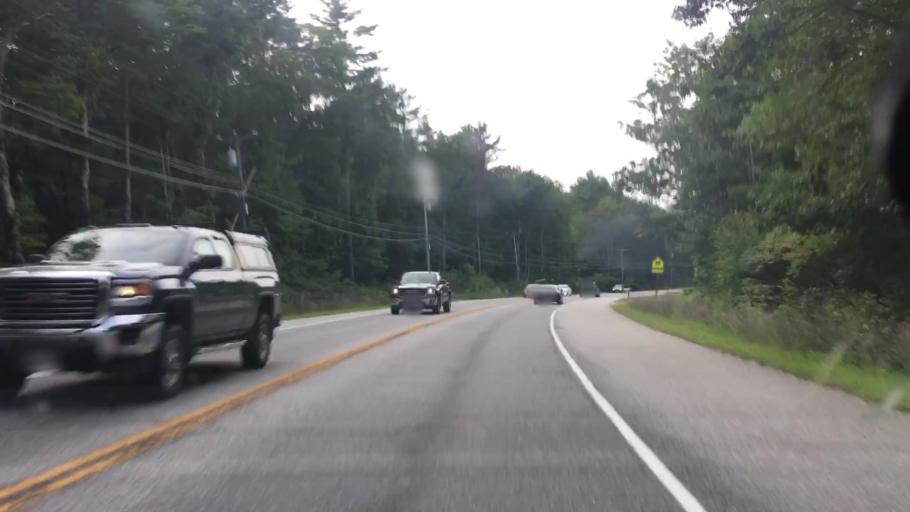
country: US
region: Maine
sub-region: Cumberland County
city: North Windham
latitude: 43.8614
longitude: -70.4640
